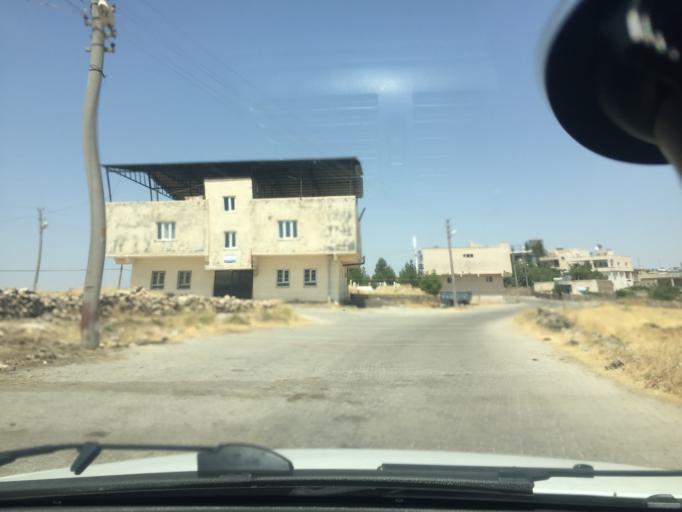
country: TR
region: Mardin
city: Kindirip
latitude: 37.4492
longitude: 41.2222
